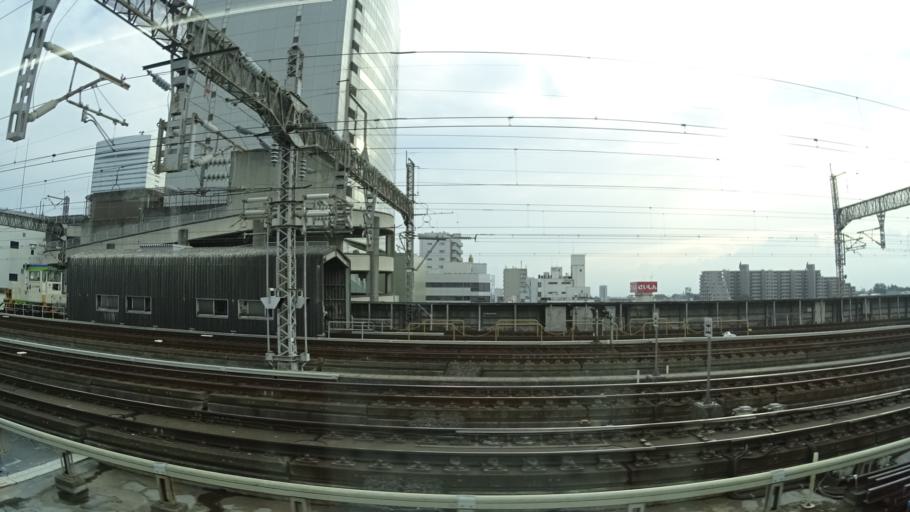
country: JP
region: Saitama
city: Yono
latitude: 35.9091
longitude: 139.6224
